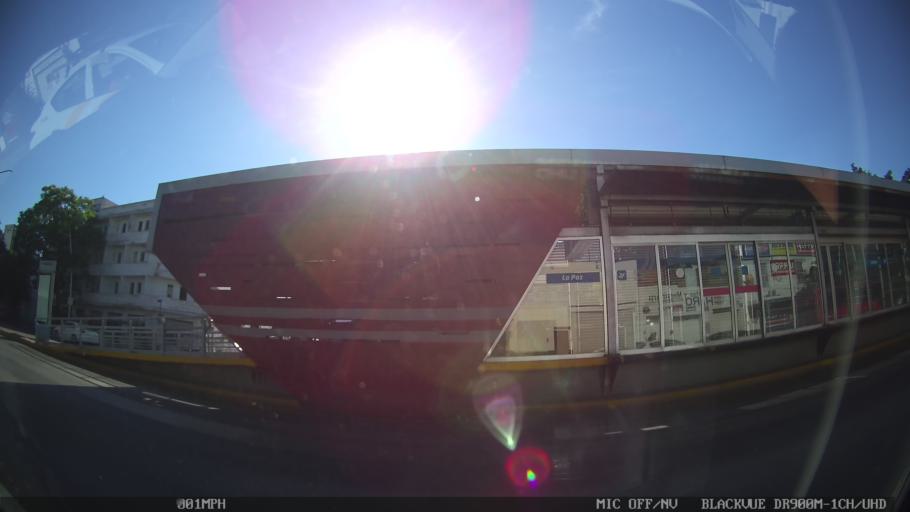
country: MX
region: Jalisco
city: Guadalajara
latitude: 20.6662
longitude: -103.3464
